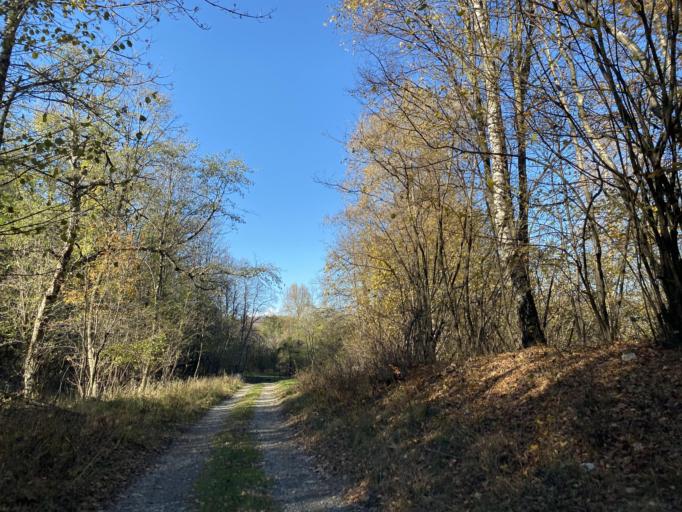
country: IT
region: Lombardy
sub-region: Provincia di Como
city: Pellio Intelvi
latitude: 45.9709
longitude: 9.0530
